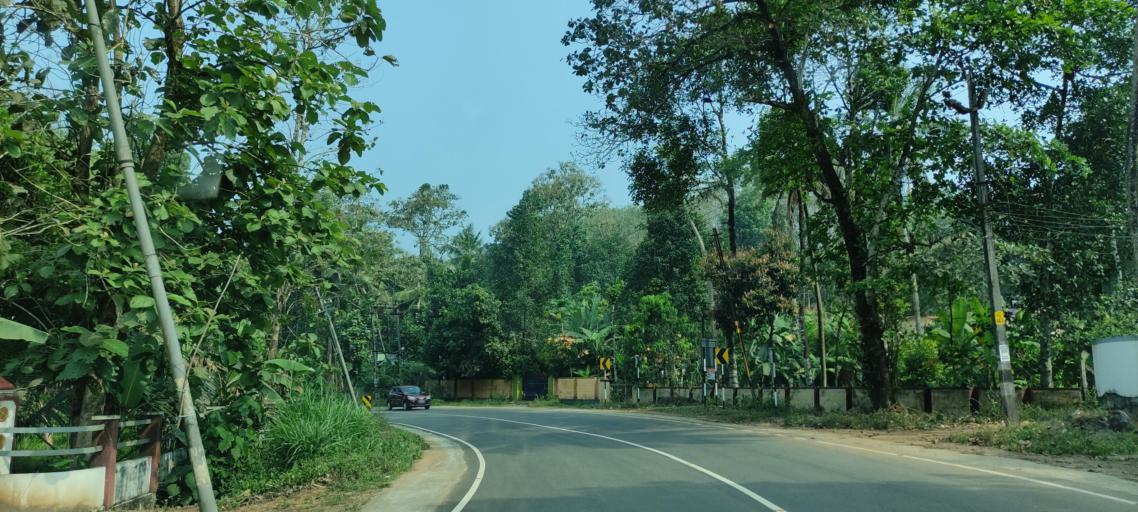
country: IN
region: Kerala
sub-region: Ernakulam
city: Piravam
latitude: 9.8005
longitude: 76.4773
